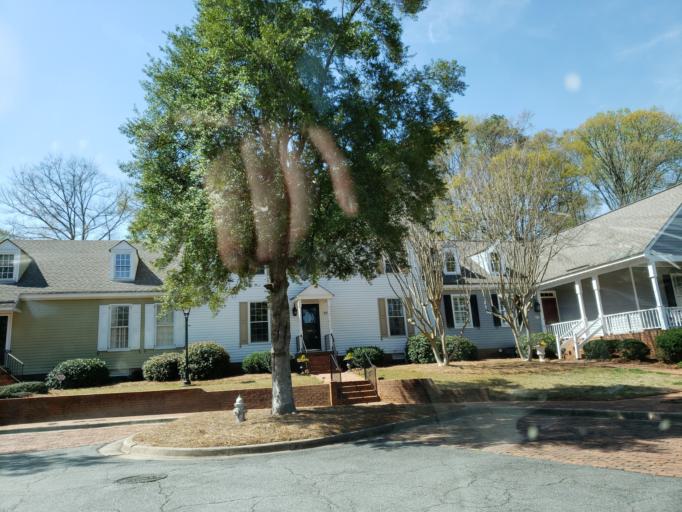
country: US
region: Georgia
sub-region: Cobb County
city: Marietta
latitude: 33.9633
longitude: -84.5606
